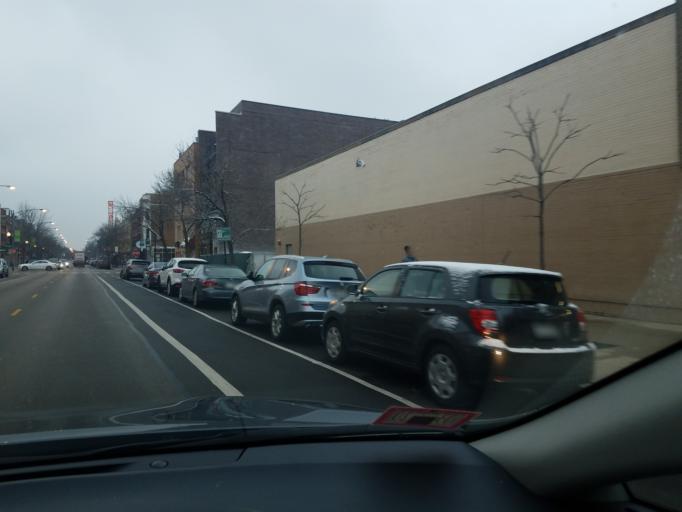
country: US
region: Illinois
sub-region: Cook County
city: Lincolnwood
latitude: 41.9482
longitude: -87.6641
